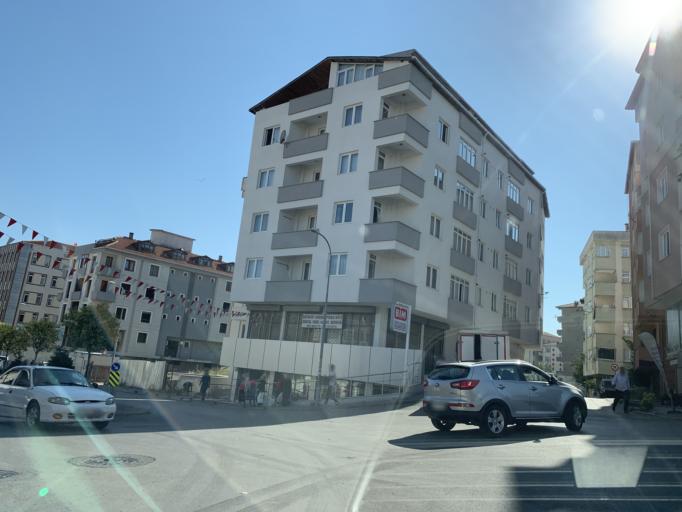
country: TR
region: Istanbul
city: Pendik
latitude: 40.8813
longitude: 29.2672
